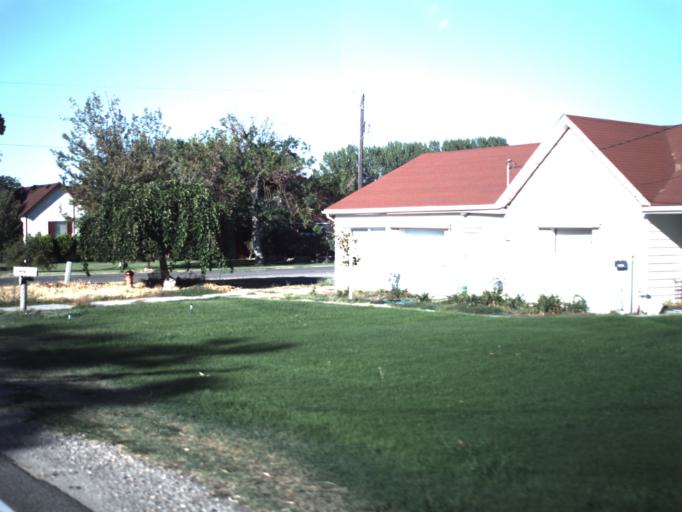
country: US
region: Utah
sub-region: Weber County
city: Hooper
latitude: 41.1786
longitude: -112.1226
